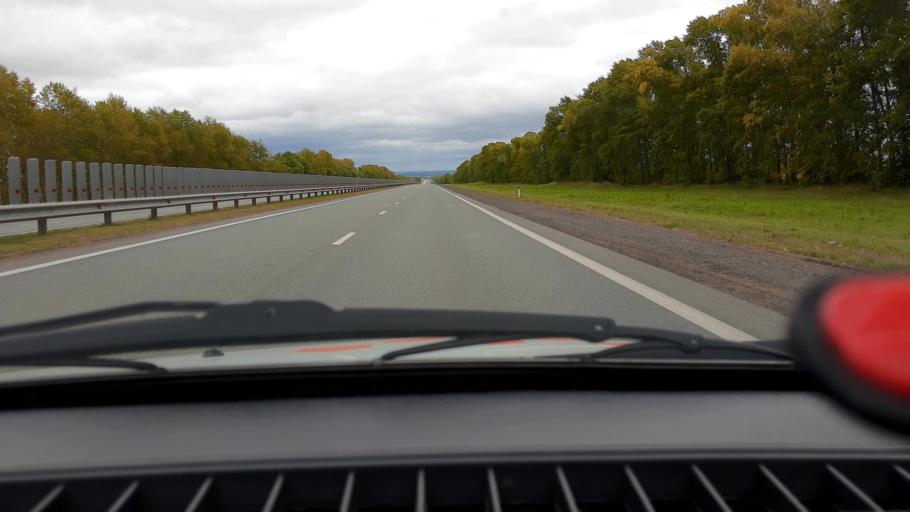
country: RU
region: Bashkortostan
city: Kushnarenkovo
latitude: 55.0369
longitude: 55.4567
